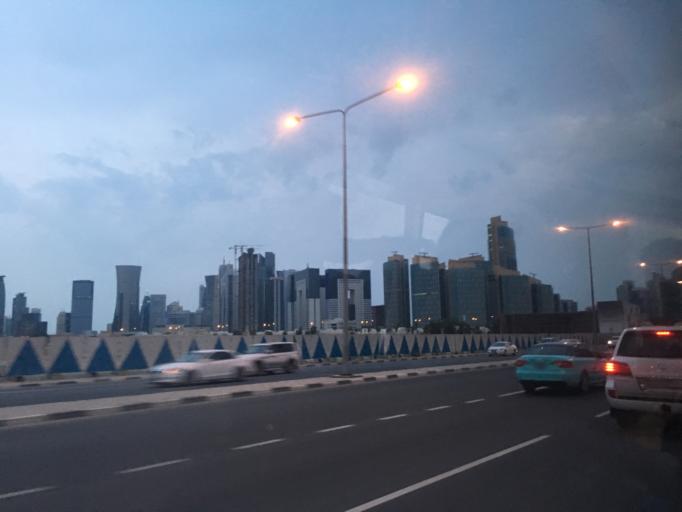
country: QA
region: Baladiyat ad Dawhah
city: Doha
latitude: 25.3223
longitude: 51.5107
